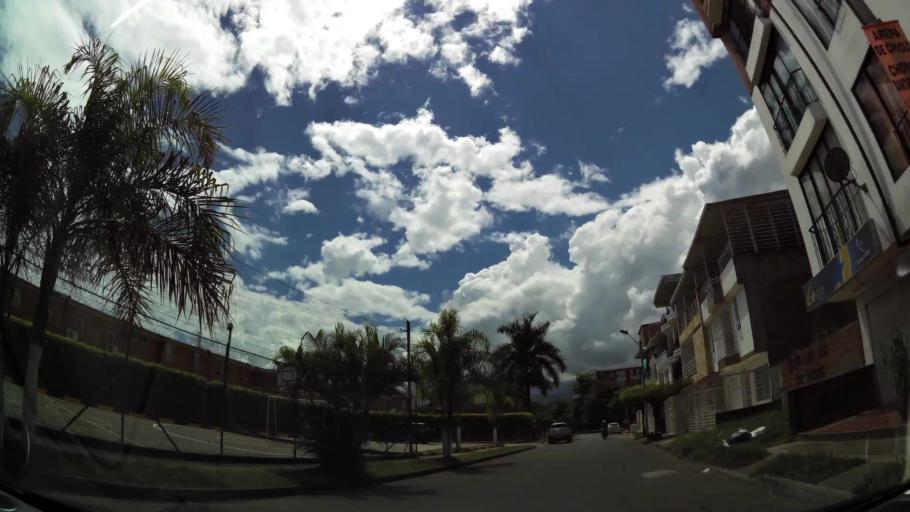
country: CO
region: Valle del Cauca
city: Cali
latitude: 3.3844
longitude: -76.5184
